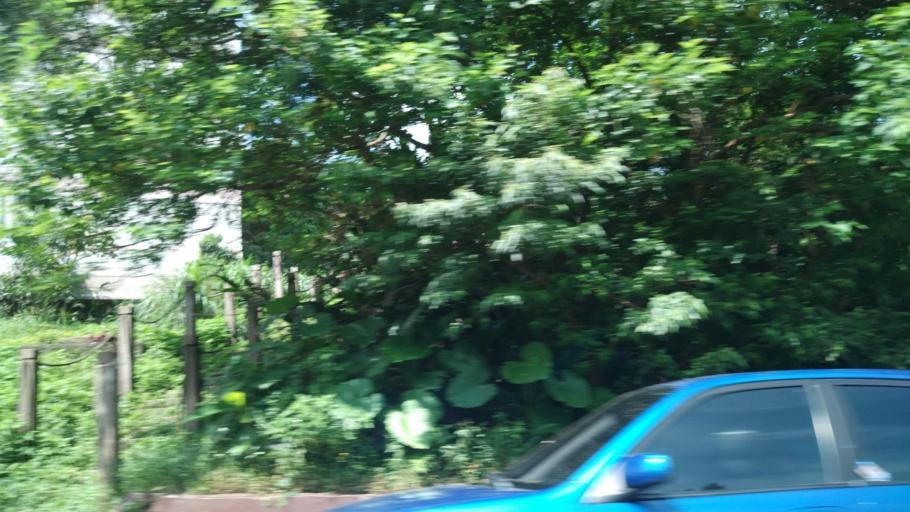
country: TW
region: Taipei
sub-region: Taipei
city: Banqiao
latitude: 24.9398
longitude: 121.5024
